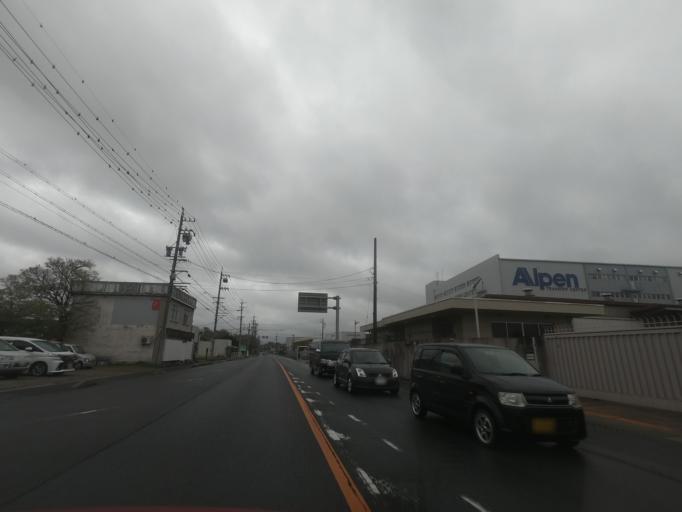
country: JP
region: Aichi
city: Kasugai
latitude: 35.2699
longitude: 137.0005
